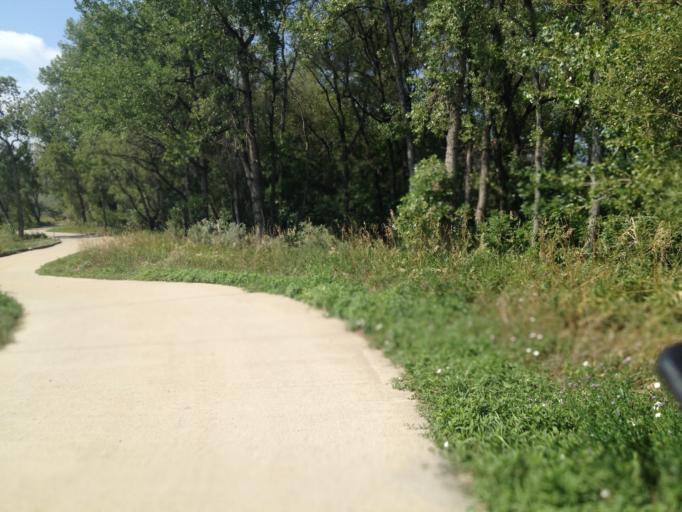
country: US
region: Colorado
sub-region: Boulder County
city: Boulder
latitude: 40.0157
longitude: -105.2149
